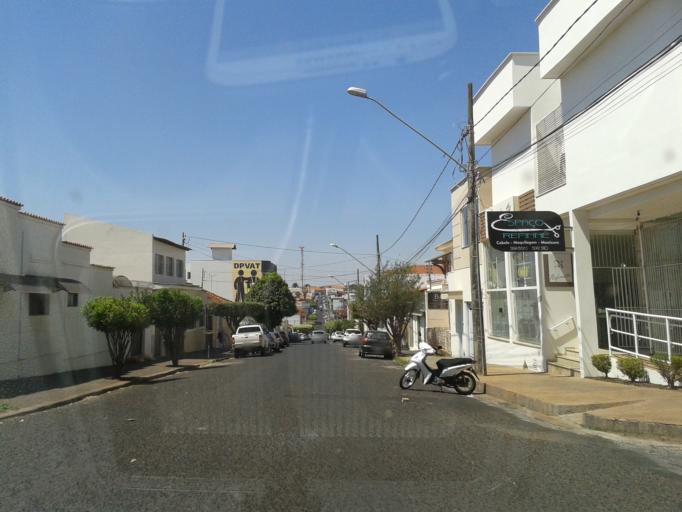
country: BR
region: Minas Gerais
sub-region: Araguari
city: Araguari
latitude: -18.6500
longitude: -48.1962
